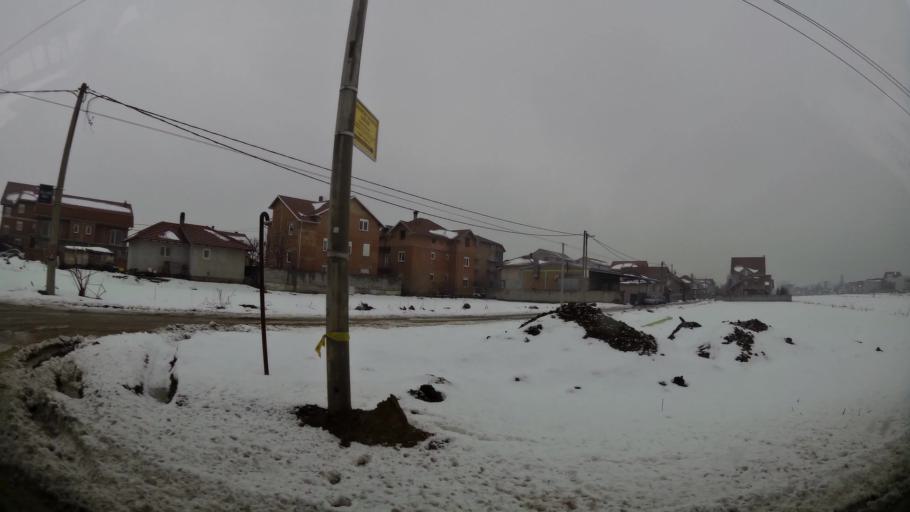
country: RS
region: Central Serbia
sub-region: Belgrade
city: Zemun
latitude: 44.8578
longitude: 20.3457
